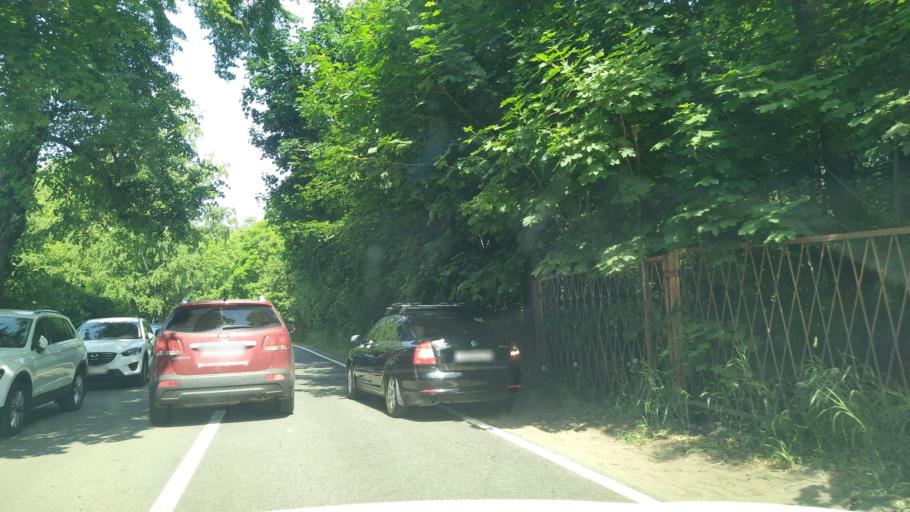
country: RU
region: St.-Petersburg
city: Kronshtadt
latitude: 60.0264
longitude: 29.6808
